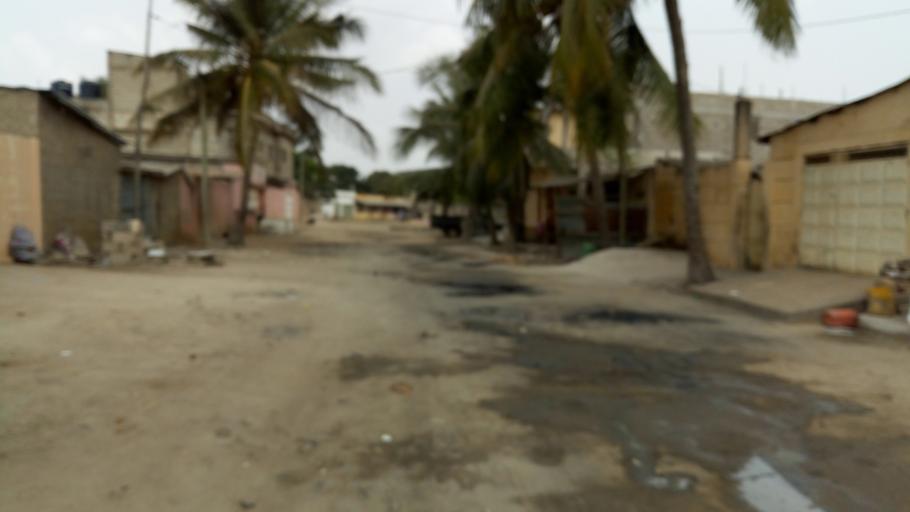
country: TG
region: Maritime
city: Lome
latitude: 6.1770
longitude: 1.1708
